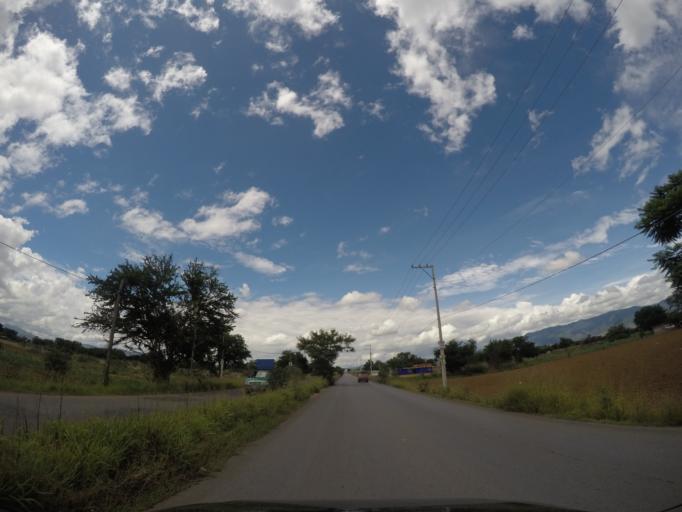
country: MX
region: Oaxaca
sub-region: Santa Cruz Xoxocotlan
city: San Isidro Monjas
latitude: 16.9930
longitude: -96.7435
